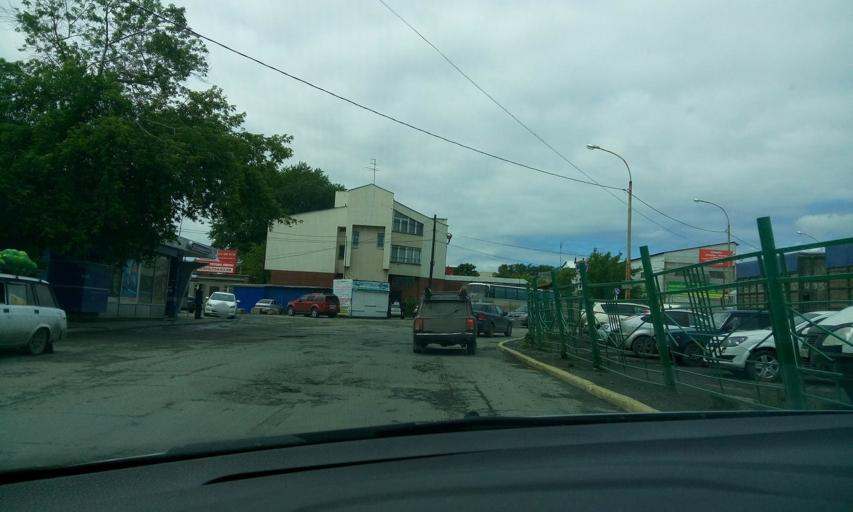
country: RU
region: Sverdlovsk
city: Yekaterinburg
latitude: 56.8637
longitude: 60.6006
